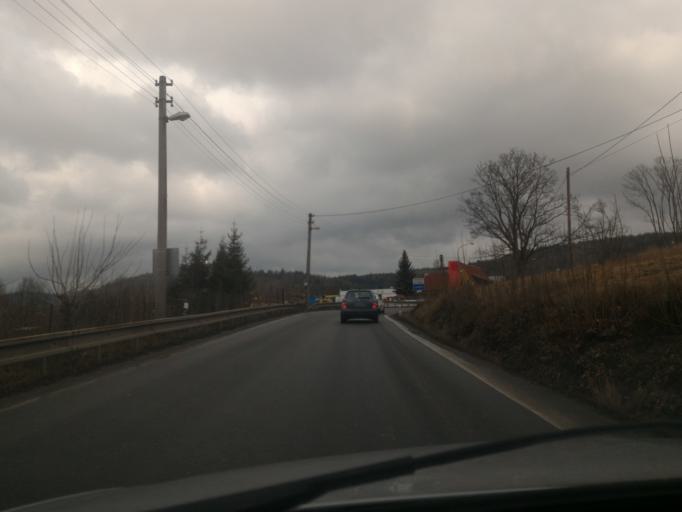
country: CZ
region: Liberecky
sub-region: Okres Jablonec nad Nisou
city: Janov nad Nisou
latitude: 50.7469
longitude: 15.1319
